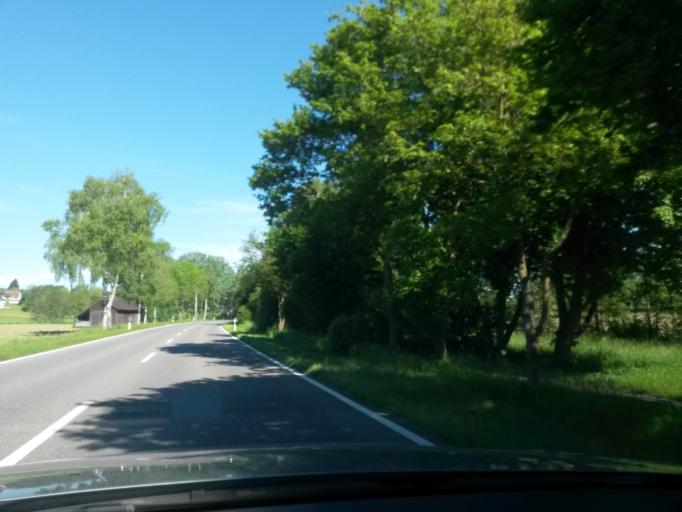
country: DE
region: Baden-Wuerttemberg
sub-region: Tuebingen Region
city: Kanzach
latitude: 48.0729
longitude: 9.5627
